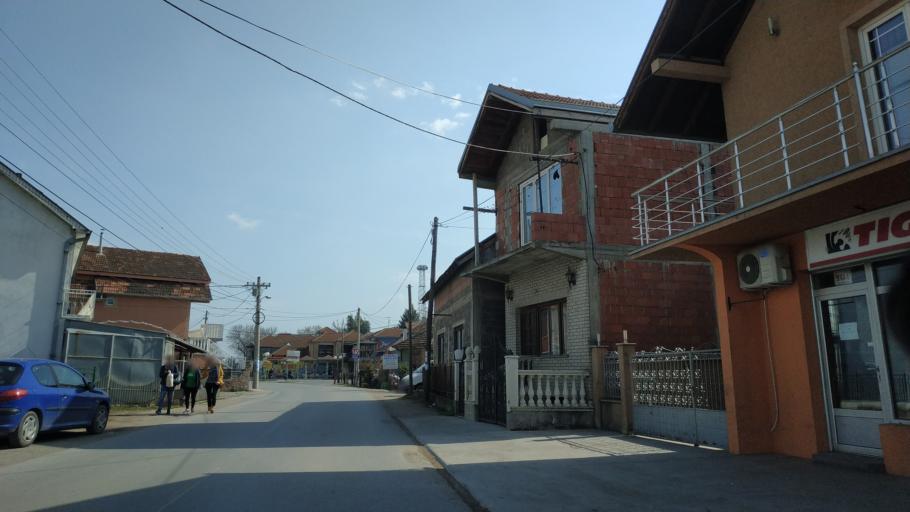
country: RS
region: Central Serbia
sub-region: Nisavski Okrug
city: Aleksinac
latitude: 43.5096
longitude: 21.6930
